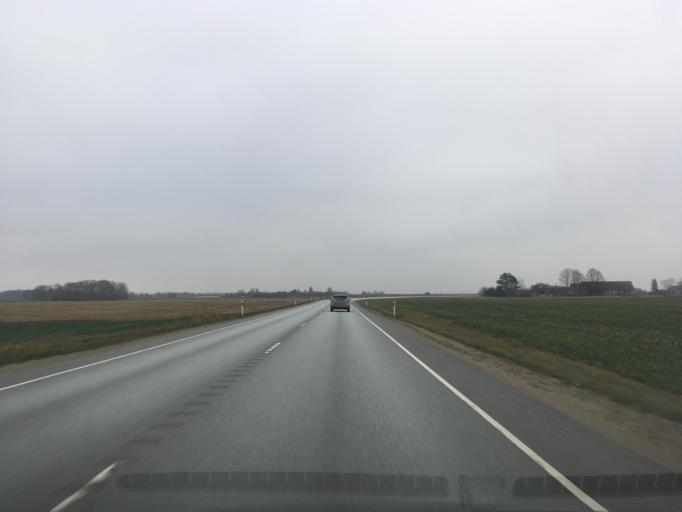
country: EE
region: Ida-Virumaa
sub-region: Puessi linn
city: Pussi
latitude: 59.4120
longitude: 27.0369
